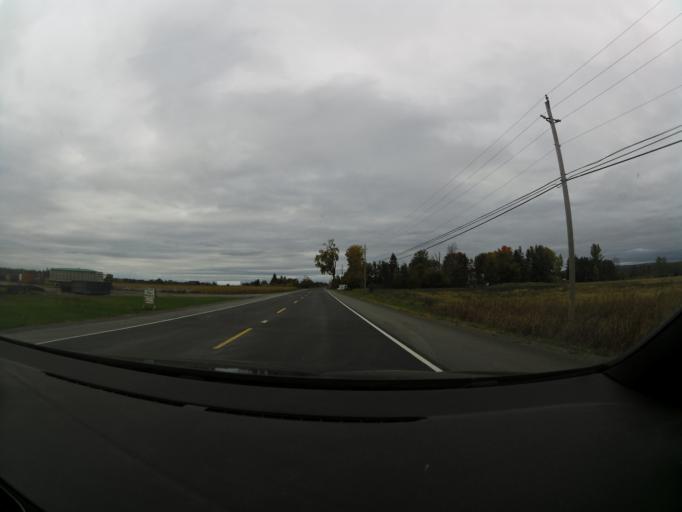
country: CA
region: Ontario
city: Bells Corners
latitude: 45.4048
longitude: -75.9994
